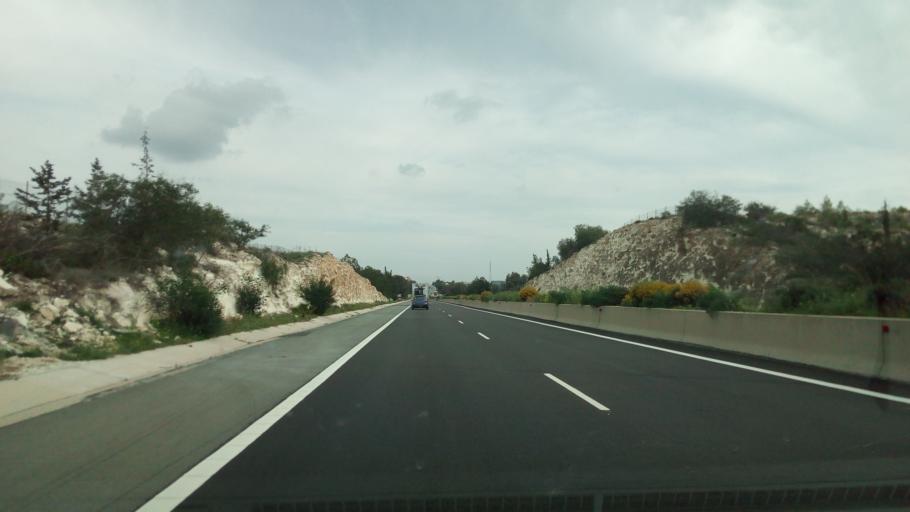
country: CY
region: Larnaka
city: Aradippou
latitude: 34.9751
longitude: 33.5365
